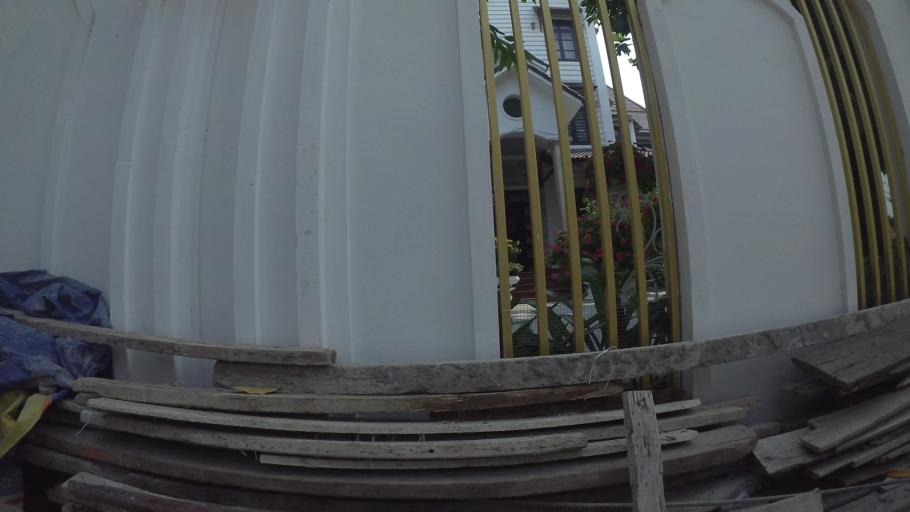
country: VN
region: Da Nang
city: Son Tra
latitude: 16.0445
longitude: 108.2455
